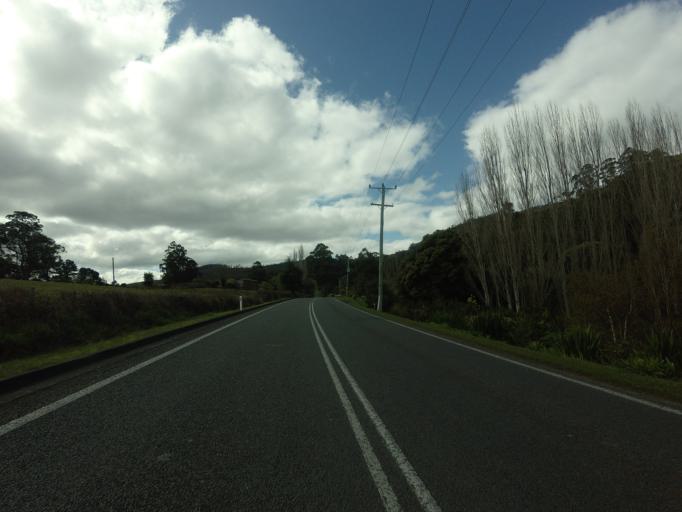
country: AU
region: Tasmania
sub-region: Huon Valley
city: Geeveston
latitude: -43.2996
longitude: 147.0084
